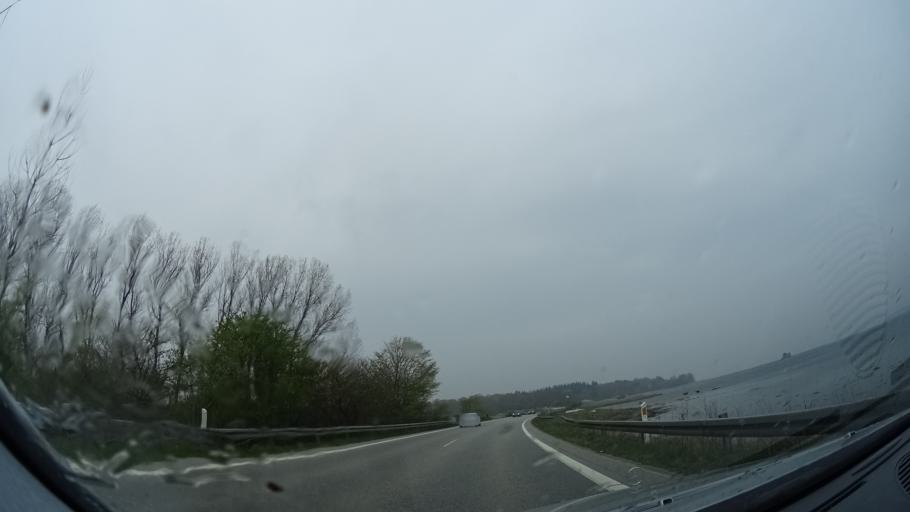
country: DK
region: Zealand
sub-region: Lejre Kommune
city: Ejby
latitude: 55.6770
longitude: 11.8053
